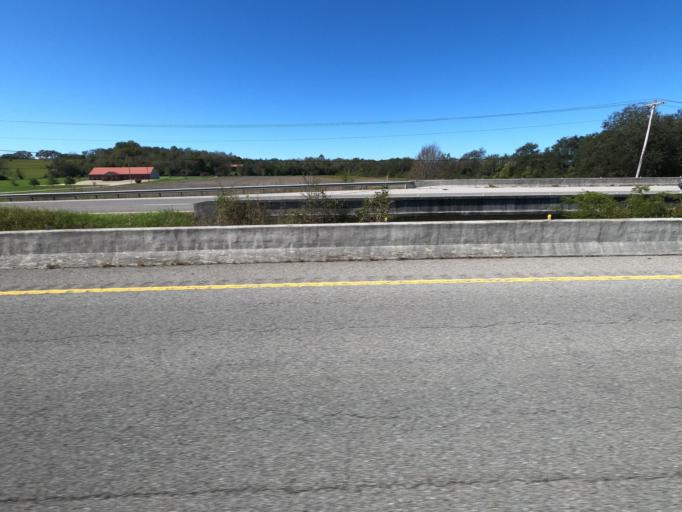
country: US
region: Tennessee
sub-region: Maury County
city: Mount Pleasant
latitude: 35.5029
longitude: -87.2315
